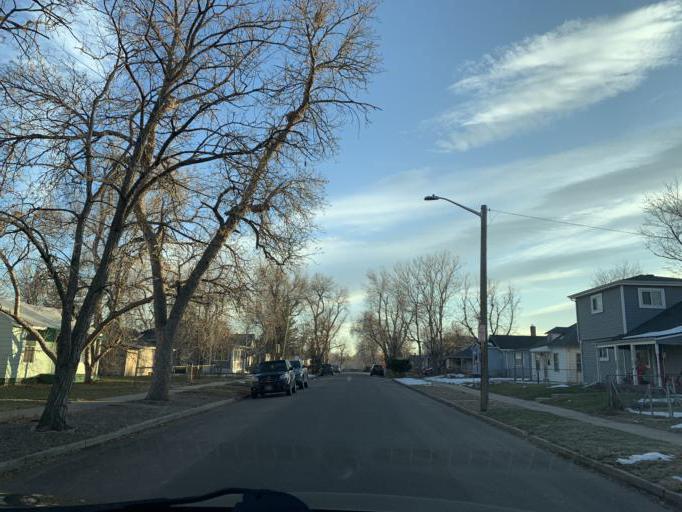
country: US
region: Colorado
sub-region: Adams County
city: Berkley
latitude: 39.7868
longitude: -105.0299
